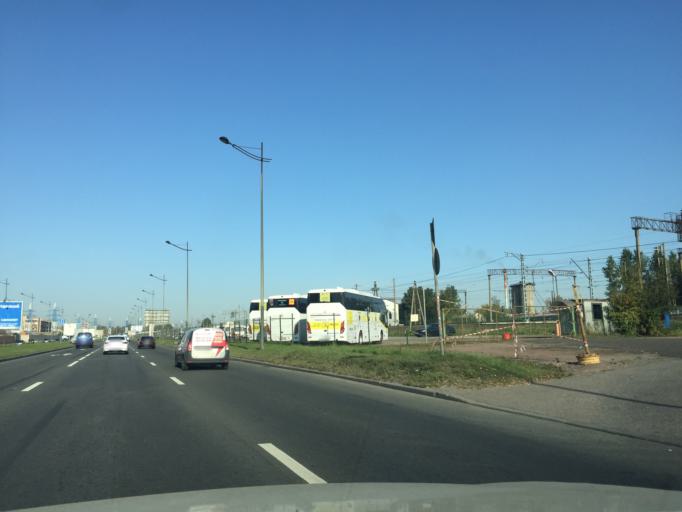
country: RU
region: St.-Petersburg
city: Kupchino
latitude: 59.8805
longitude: 30.3475
